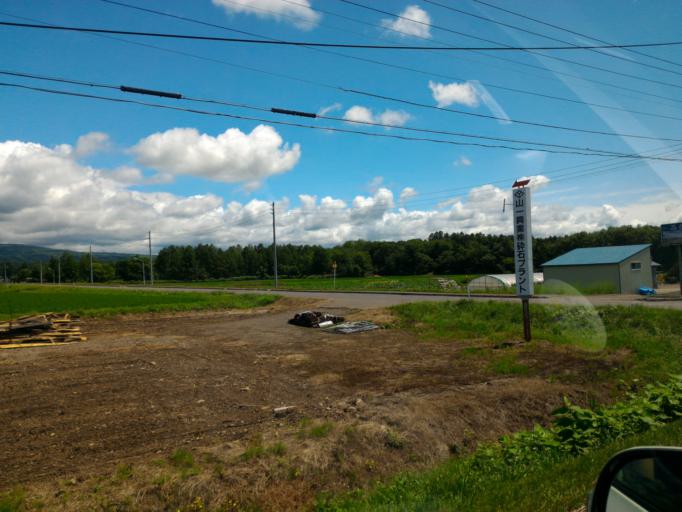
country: JP
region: Hokkaido
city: Nayoro
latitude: 44.5126
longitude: 142.3316
